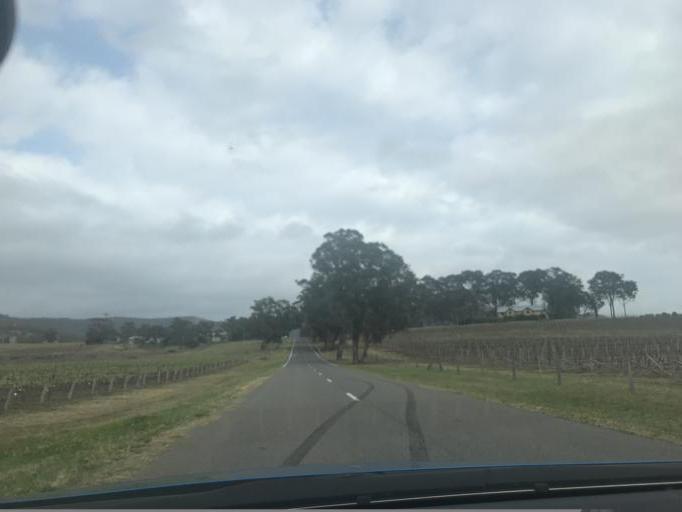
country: AU
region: New South Wales
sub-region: Cessnock
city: Cessnock
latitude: -32.8089
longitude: 151.2898
